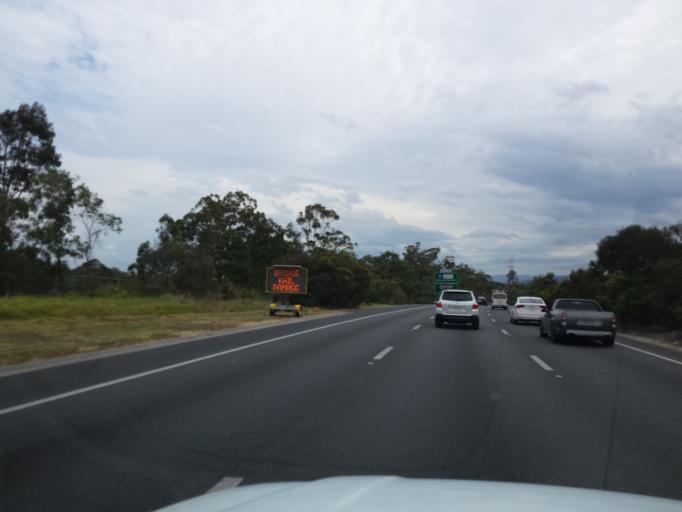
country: AU
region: Queensland
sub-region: Gold Coast
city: Nerang
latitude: -27.9716
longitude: 153.3471
